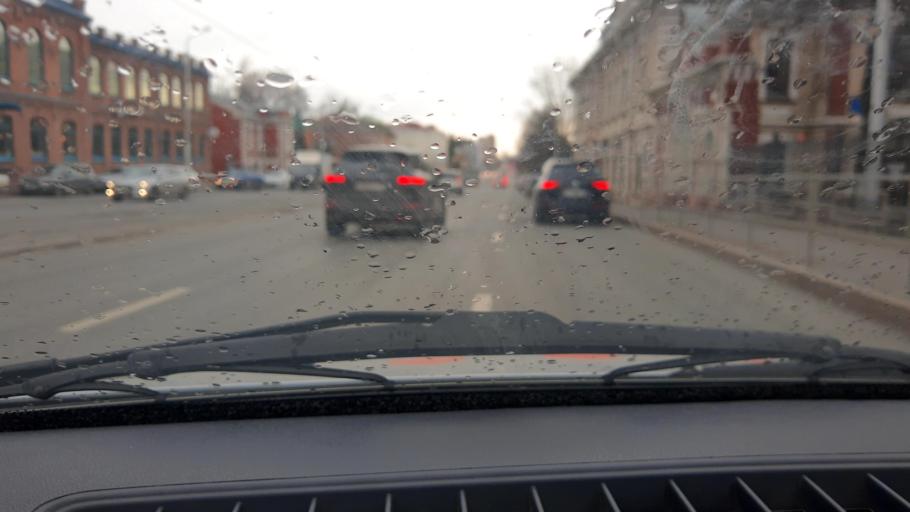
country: RU
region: Bashkortostan
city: Ufa
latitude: 54.7362
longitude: 55.9491
